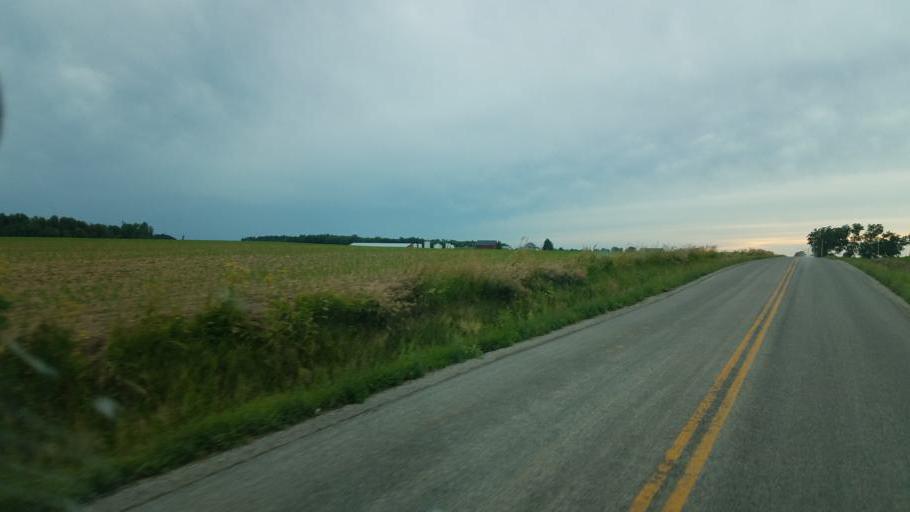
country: US
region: Ohio
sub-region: Ashland County
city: Ashland
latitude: 40.9533
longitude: -82.4132
